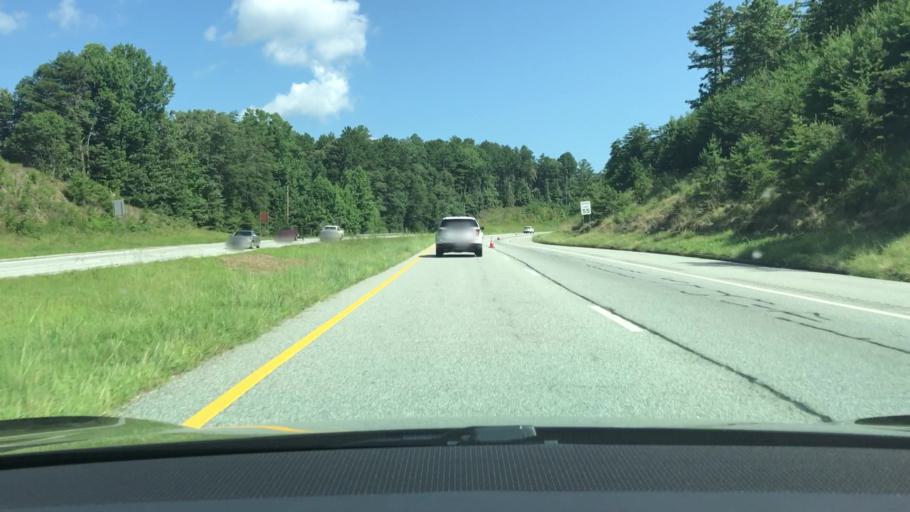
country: US
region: Georgia
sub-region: Rabun County
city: Clayton
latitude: 34.7451
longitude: -83.4012
